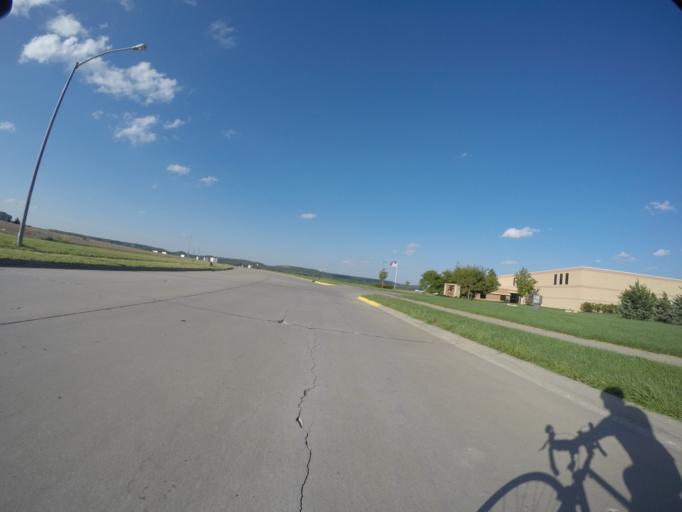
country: US
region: Kansas
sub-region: Riley County
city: Ogden
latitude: 39.1404
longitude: -96.6770
